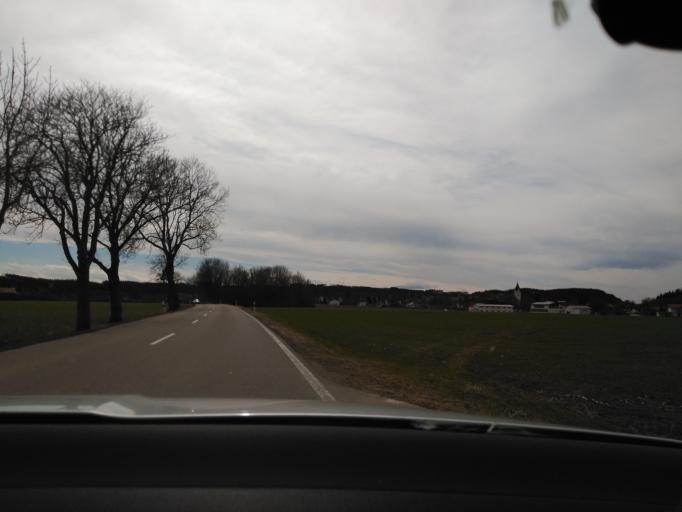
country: DE
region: Baden-Wuerttemberg
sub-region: Tuebingen Region
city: Aichstetten
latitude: 47.9018
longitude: 10.0879
